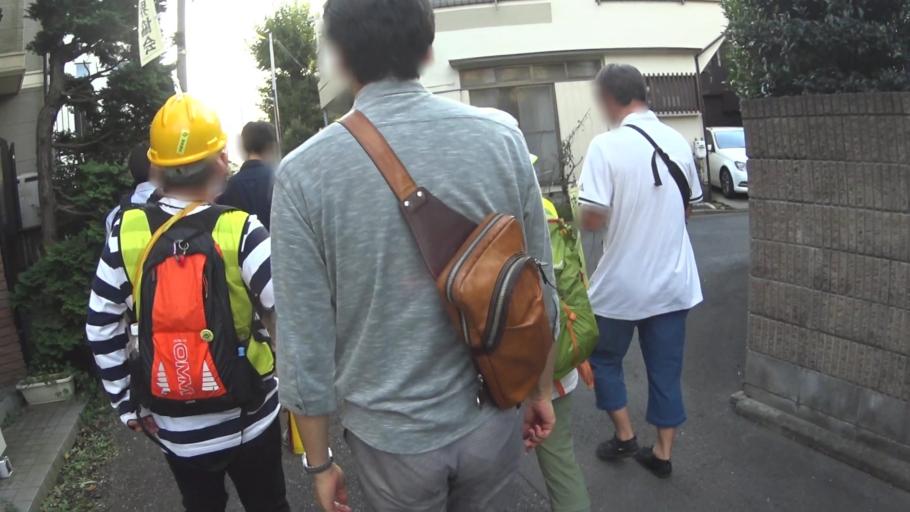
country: JP
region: Tokyo
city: Tanashicho
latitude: 35.7543
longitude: 139.5441
